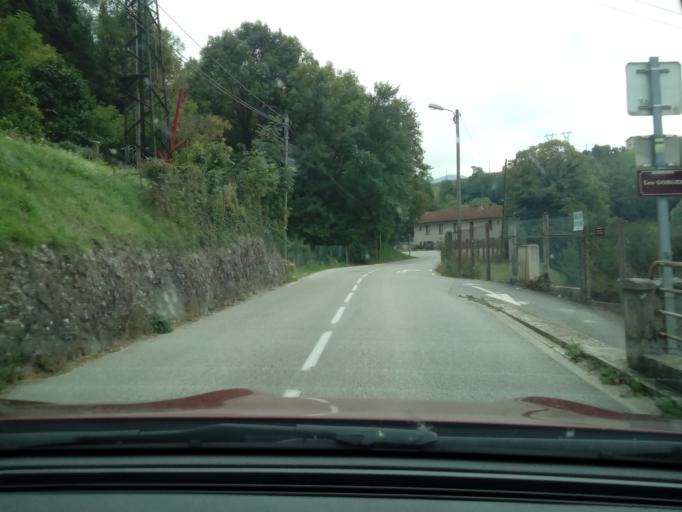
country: FR
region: Rhone-Alpes
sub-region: Departement de l'Isere
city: Pont-en-Royans
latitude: 45.0586
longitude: 5.3440
